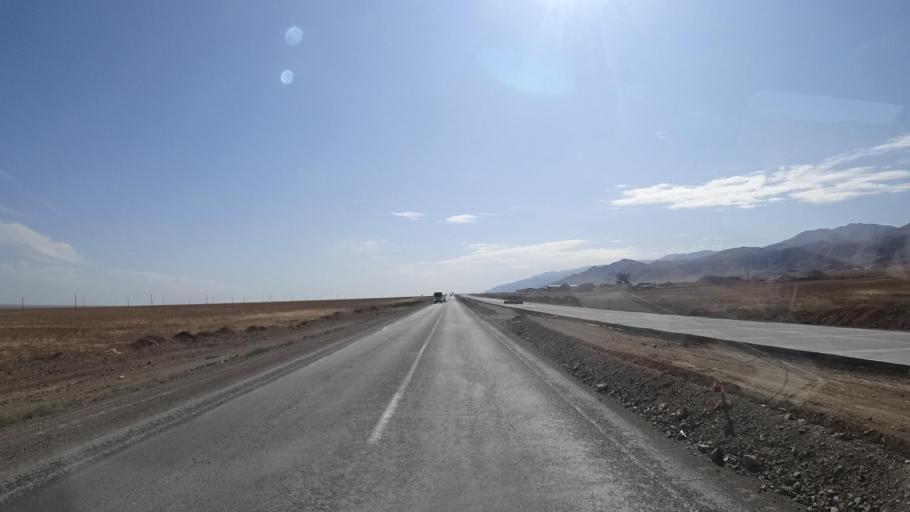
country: KG
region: Chuy
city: Ivanovka
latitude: 43.3932
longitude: 75.1345
